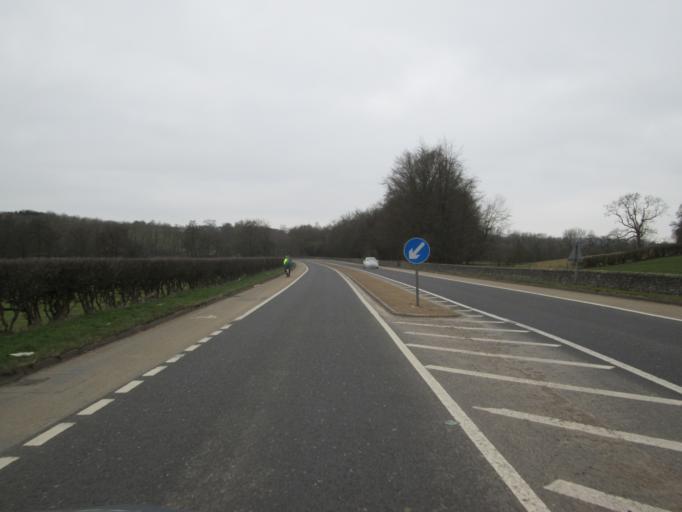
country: GB
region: England
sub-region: Derbyshire
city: Bakewell
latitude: 53.1896
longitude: -1.6368
